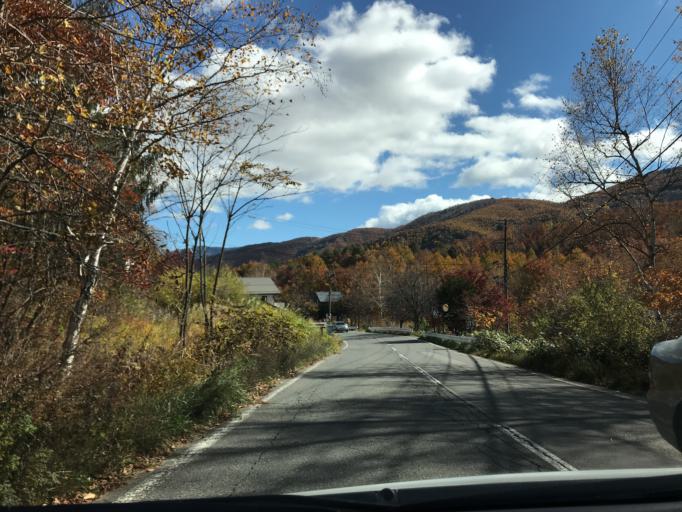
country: JP
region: Nagano
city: Toyoshina
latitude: 36.1239
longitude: 137.6418
